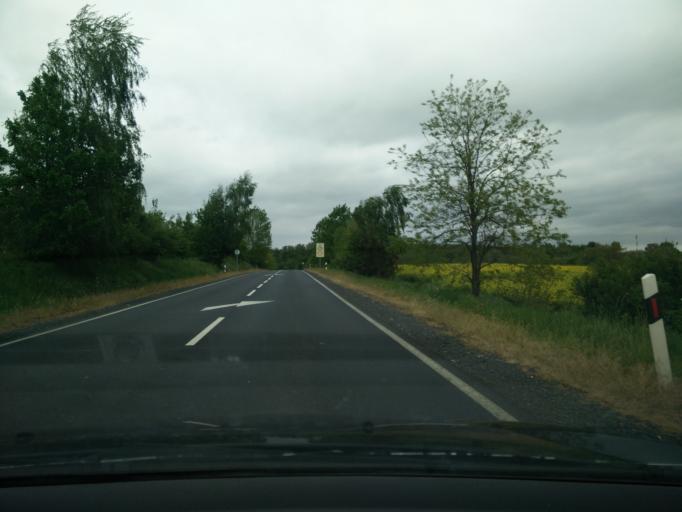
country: HU
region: Zala
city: Turje
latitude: 46.9816
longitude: 17.1201
